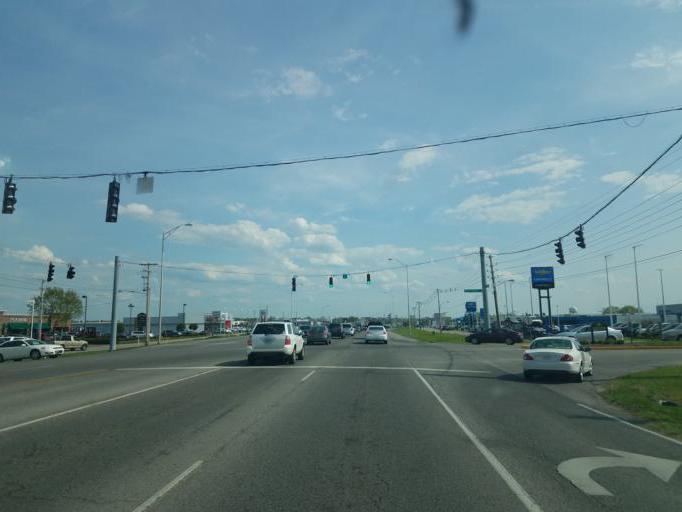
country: US
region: Kentucky
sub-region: Warren County
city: Bowling Green
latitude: 36.9597
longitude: -86.4294
